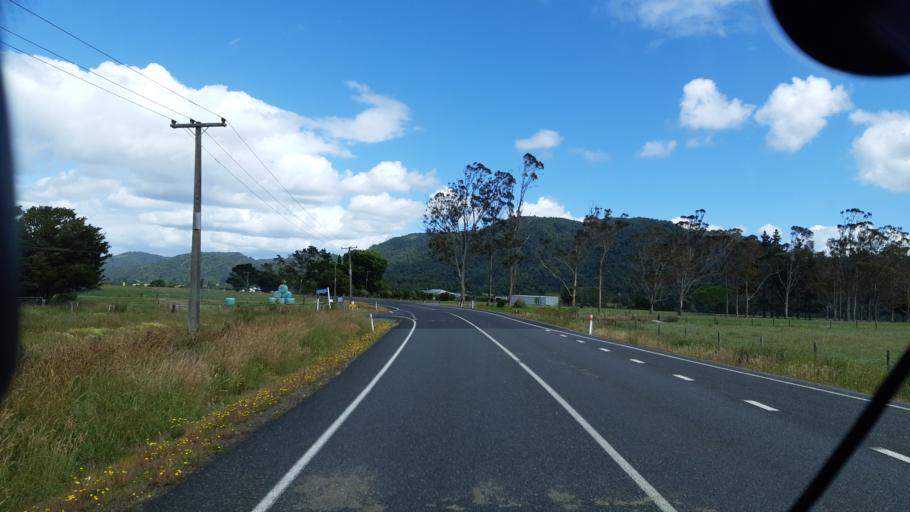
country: NZ
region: Northland
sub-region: Far North District
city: Waimate North
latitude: -35.2871
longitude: 173.7051
